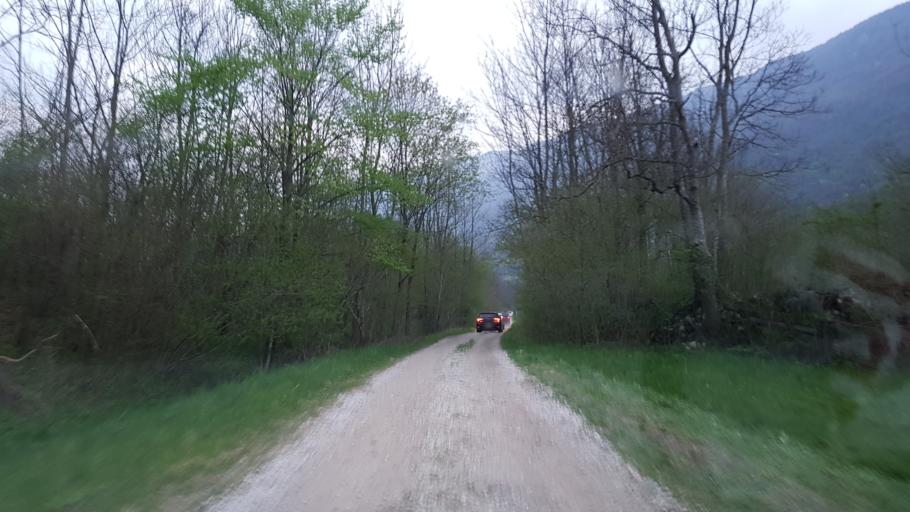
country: SI
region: Kobarid
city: Kobarid
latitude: 46.2424
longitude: 13.5282
